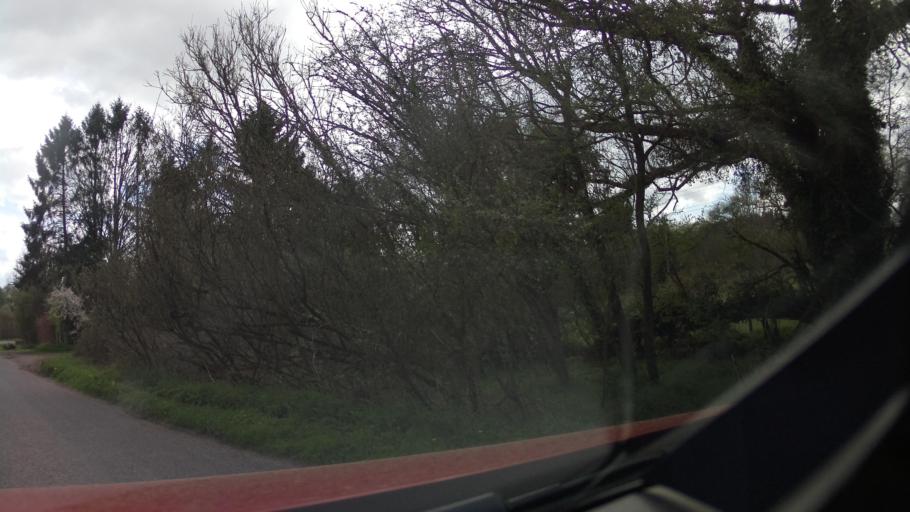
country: GB
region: England
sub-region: Hampshire
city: Highclere
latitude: 51.2912
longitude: -1.4438
